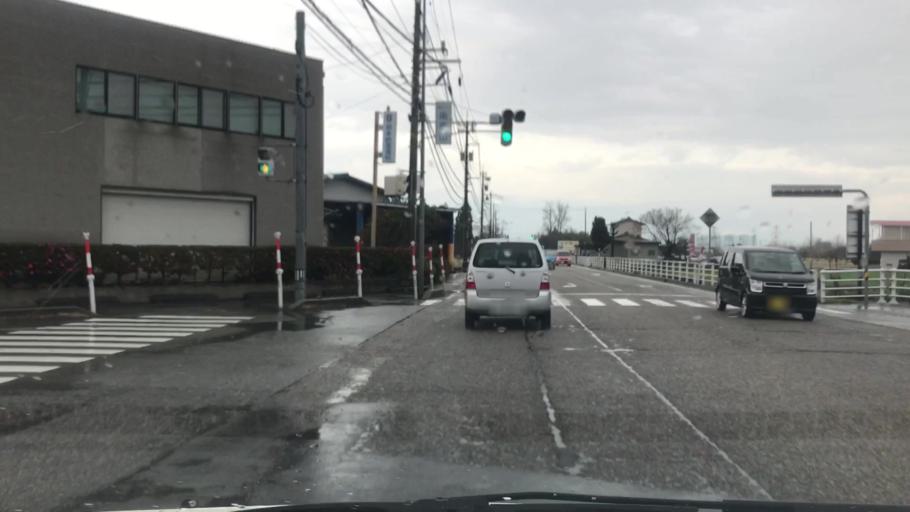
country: JP
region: Toyama
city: Toyama-shi
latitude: 36.6210
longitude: 137.2052
